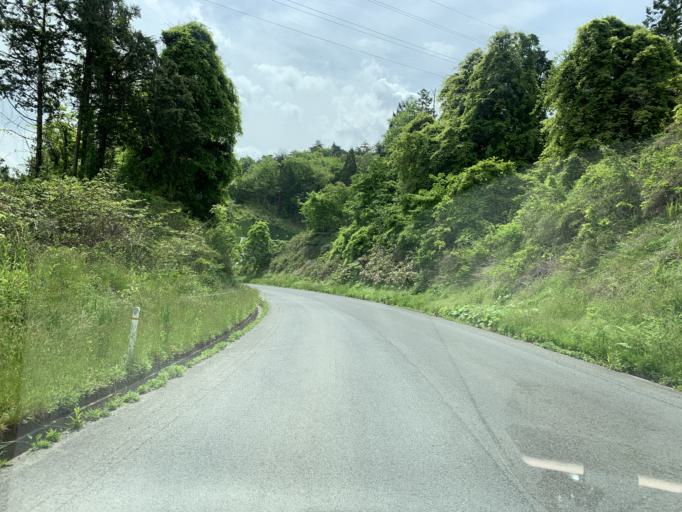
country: JP
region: Iwate
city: Ichinoseki
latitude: 38.8598
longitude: 140.9837
